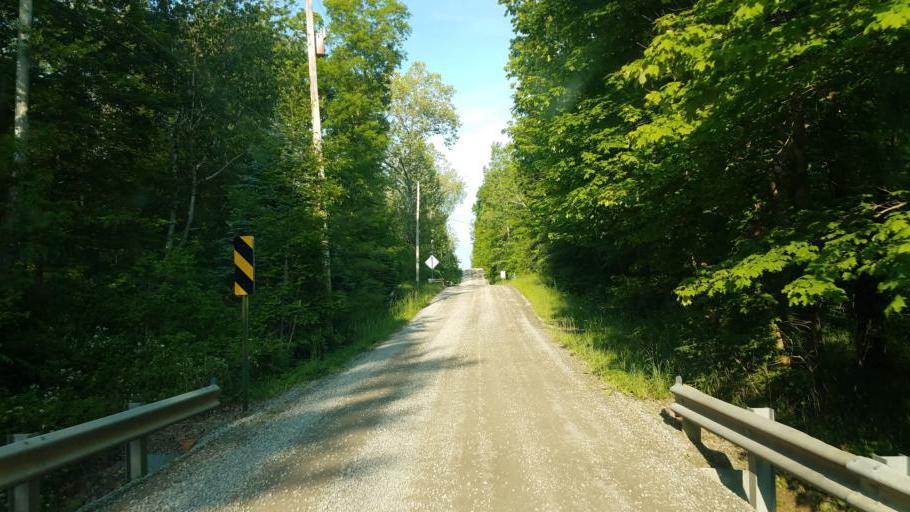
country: US
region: Ohio
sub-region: Morrow County
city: Mount Gilead
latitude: 40.4325
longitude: -82.7712
